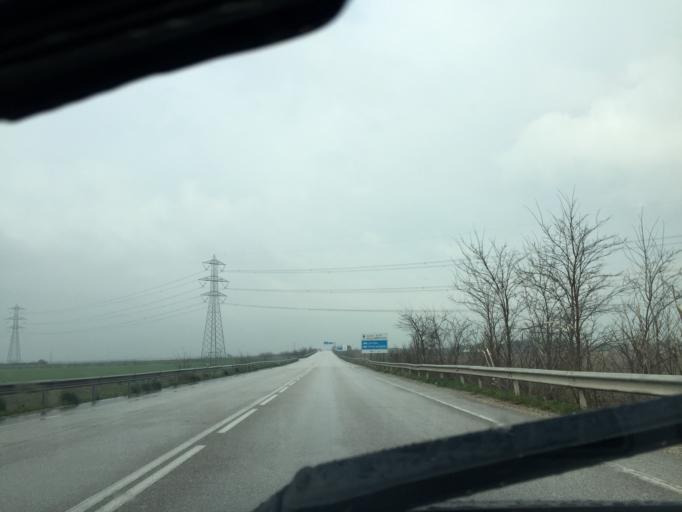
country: IT
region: Apulia
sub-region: Provincia di Foggia
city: Foggia
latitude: 41.4981
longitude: 15.5285
